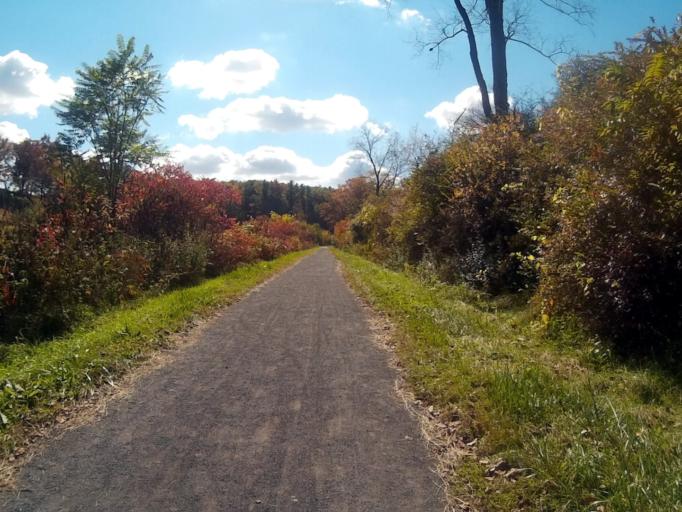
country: US
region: Pennsylvania
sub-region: Centre County
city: State College
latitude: 40.8118
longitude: -77.8752
